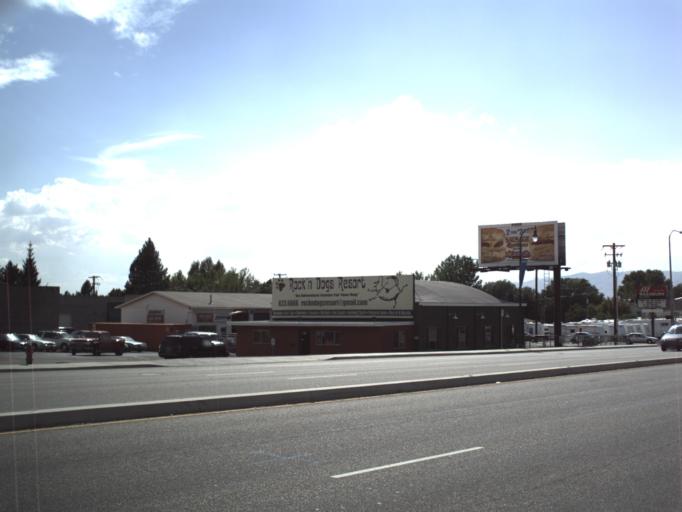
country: US
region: Utah
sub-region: Utah County
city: Orem
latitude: 40.3121
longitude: -111.7014
